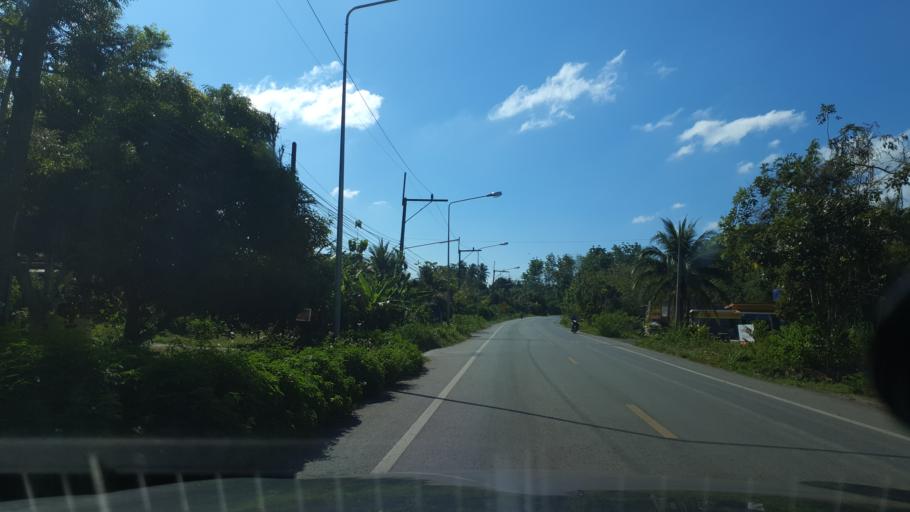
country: TH
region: Phangnga
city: Ban Ao Nang
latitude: 8.0682
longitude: 98.8091
